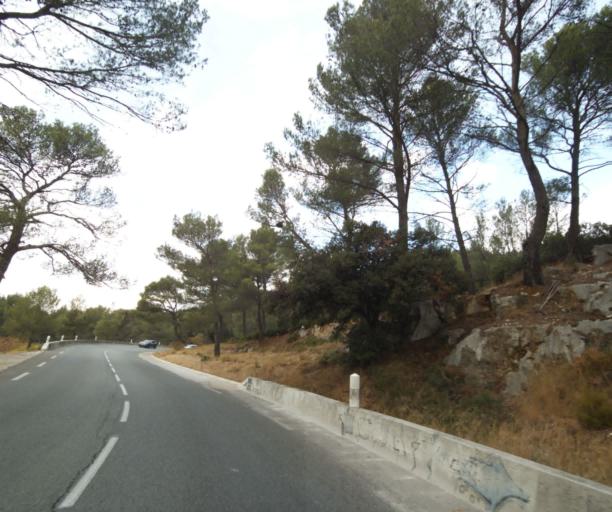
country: FR
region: Provence-Alpes-Cote d'Azur
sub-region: Departement des Bouches-du-Rhone
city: Cuges-les-Pins
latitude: 43.2650
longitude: 5.6658
